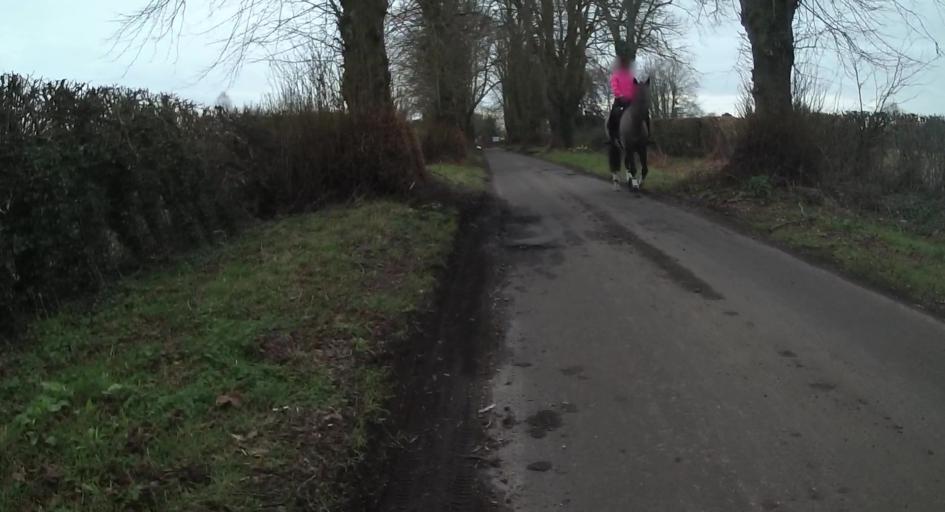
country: GB
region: England
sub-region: Hampshire
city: Overton
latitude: 51.2568
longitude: -1.1835
